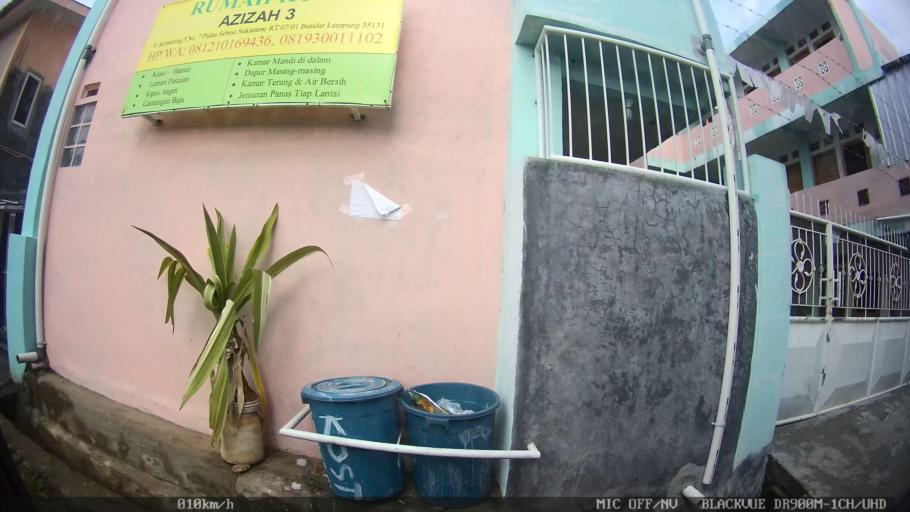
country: ID
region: Lampung
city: Kedaton
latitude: -5.3874
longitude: 105.3019
